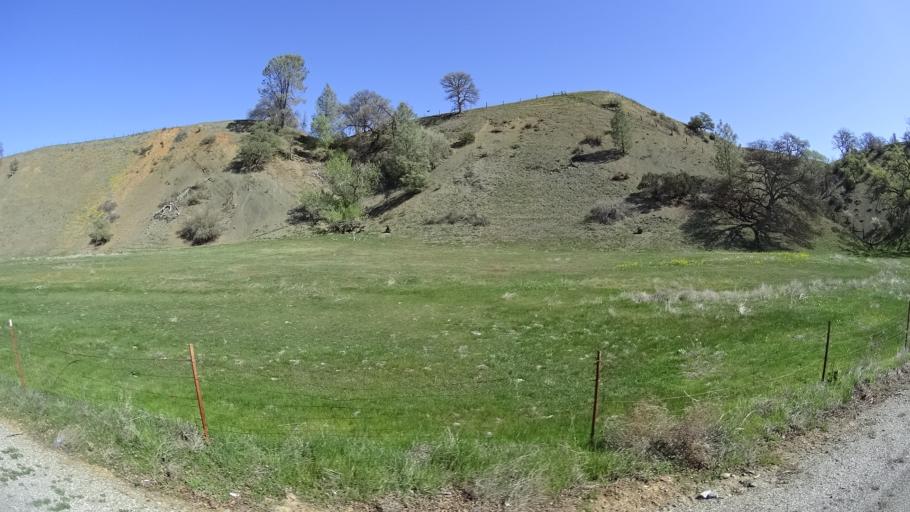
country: US
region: California
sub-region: Glenn County
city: Orland
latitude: 39.6790
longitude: -122.5253
